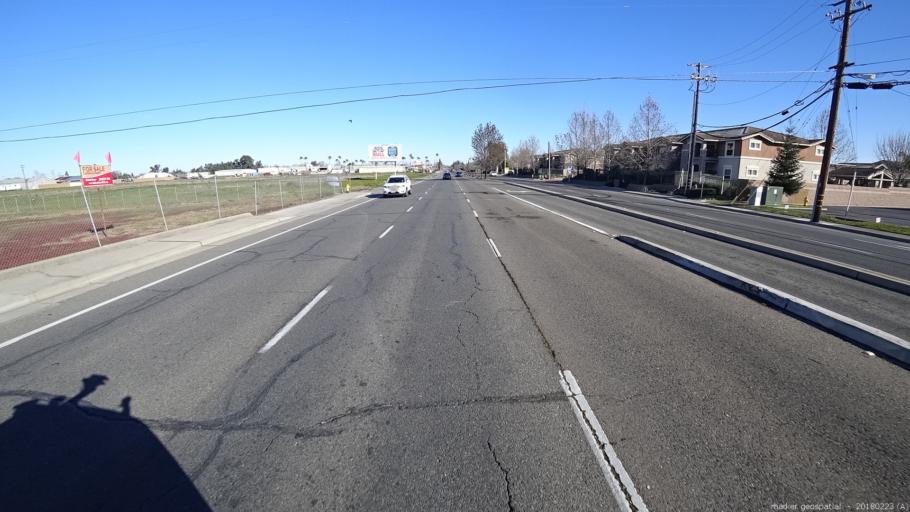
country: US
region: California
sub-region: Sacramento County
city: North Highlands
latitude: 38.6919
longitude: -121.3830
